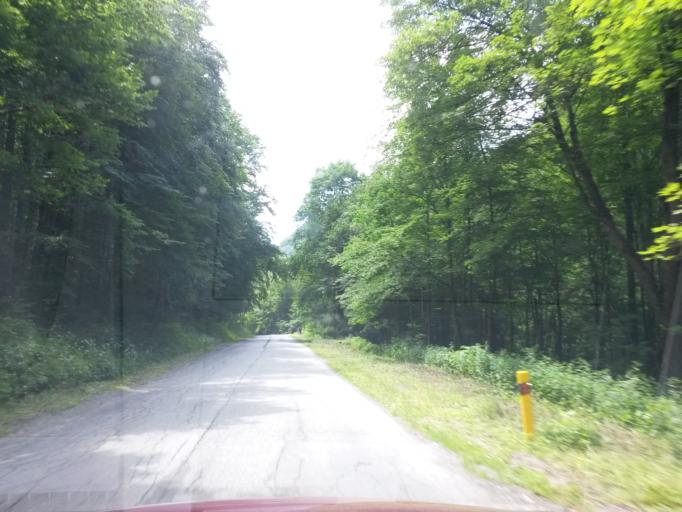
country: SK
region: Kosicky
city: Gelnica
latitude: 48.9176
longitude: 21.0338
